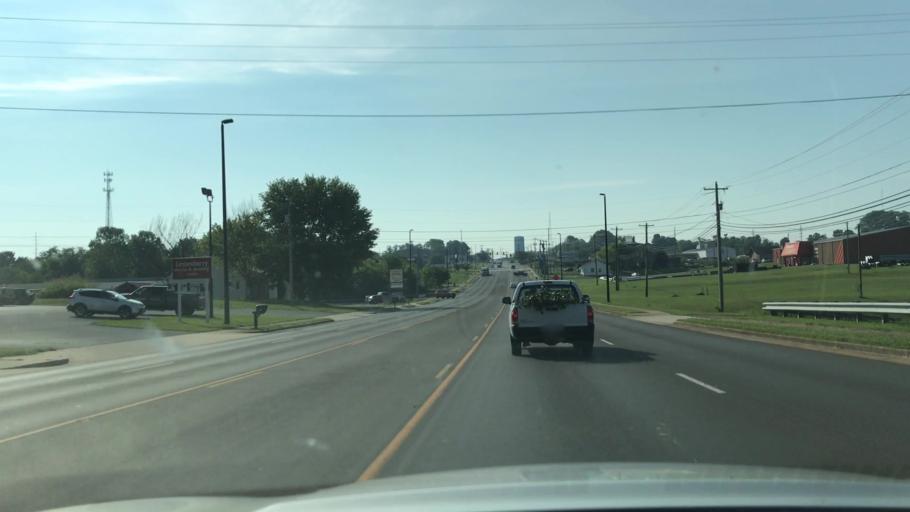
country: US
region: Kentucky
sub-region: Barren County
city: Glasgow
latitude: 37.0045
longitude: -85.9305
